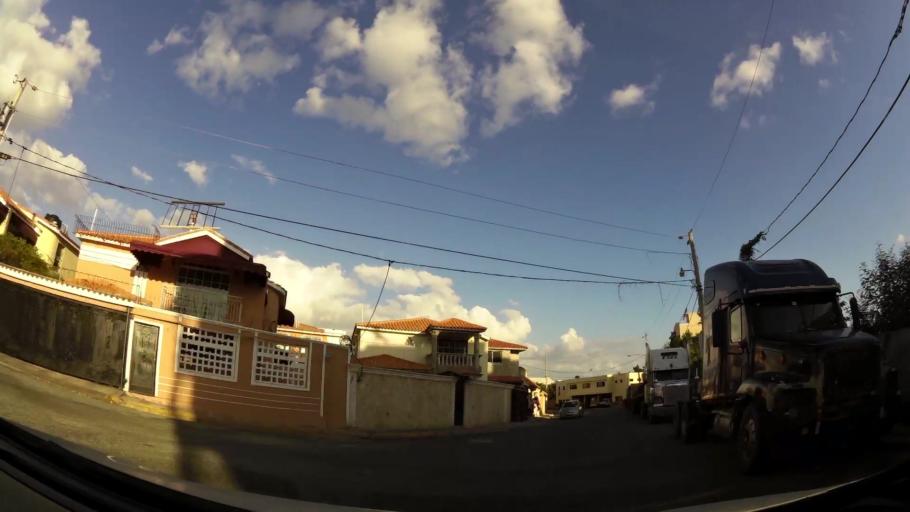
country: DO
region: Santo Domingo
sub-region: Santo Domingo
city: Santo Domingo Este
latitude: 18.4784
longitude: -69.8329
